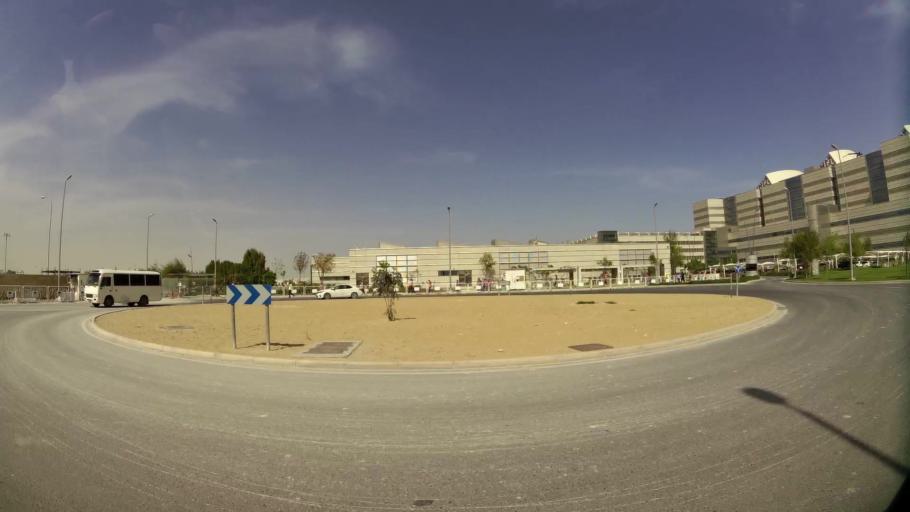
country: QA
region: Baladiyat ar Rayyan
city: Ar Rayyan
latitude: 25.3231
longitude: 51.4422
